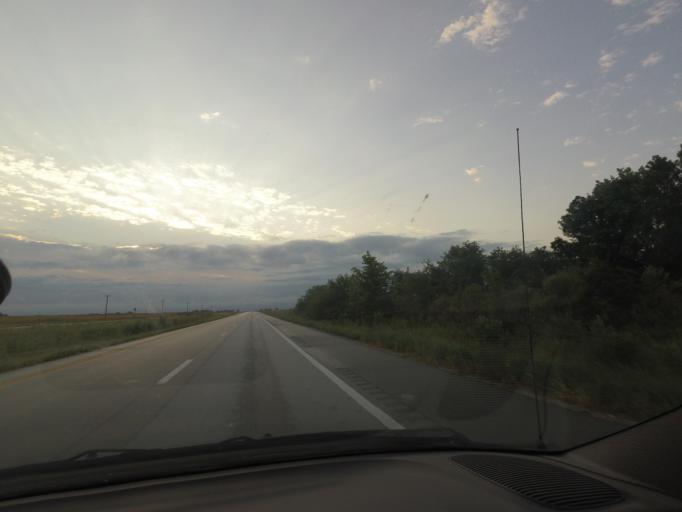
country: US
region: Missouri
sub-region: Shelby County
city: Shelbina
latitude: 39.7152
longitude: -92.1322
